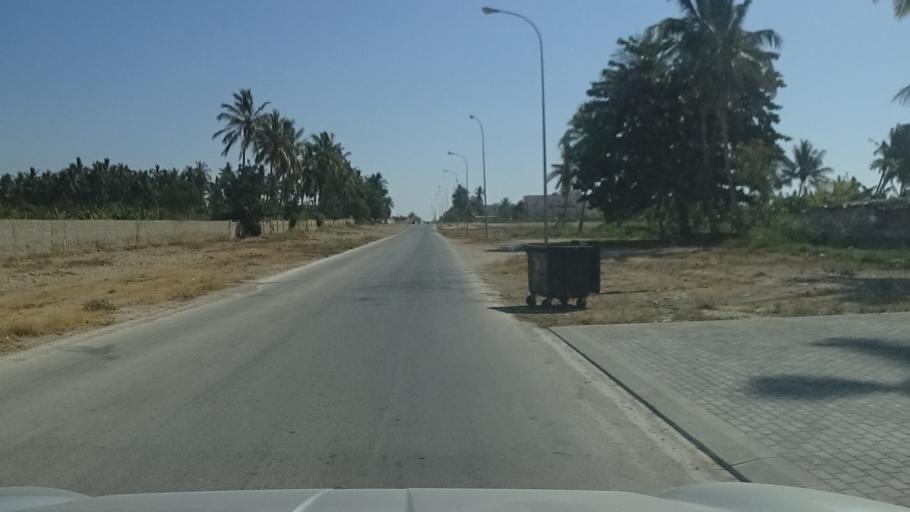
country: OM
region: Zufar
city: Salalah
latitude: 17.0342
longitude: 54.1542
